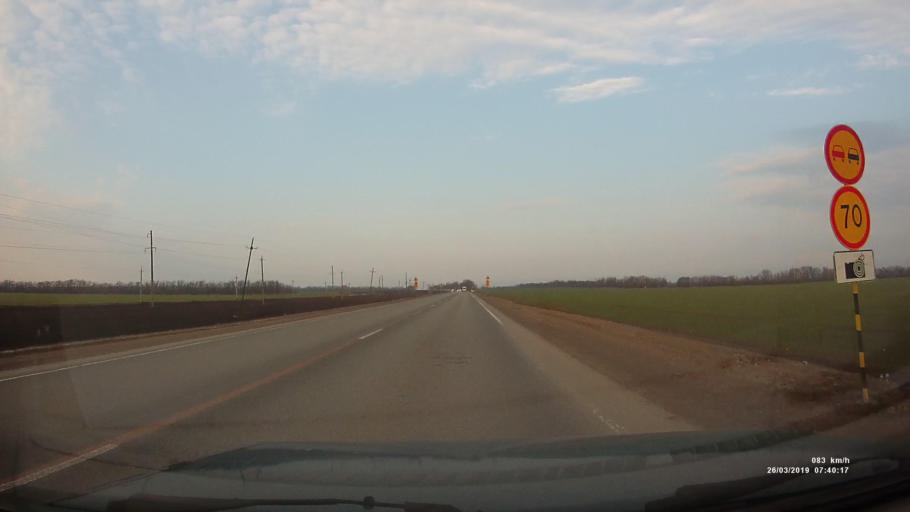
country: RU
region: Rostov
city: Novobessergenovka
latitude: 47.1954
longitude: 38.6501
